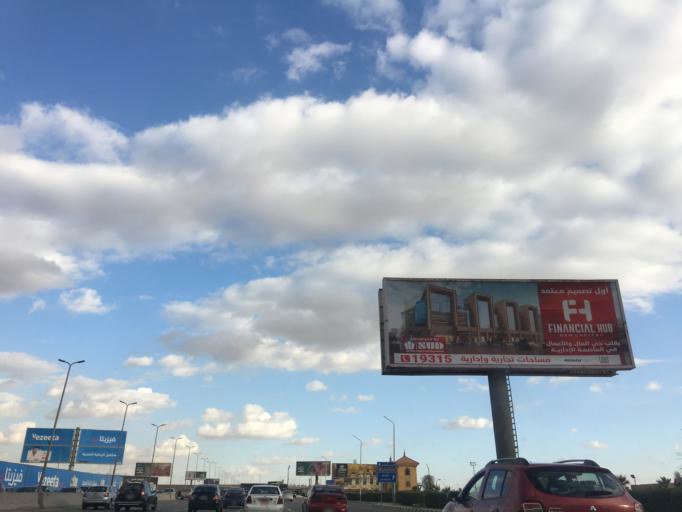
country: EG
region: Muhafazat al Qahirah
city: Cairo
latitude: 30.0240
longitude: 31.3640
